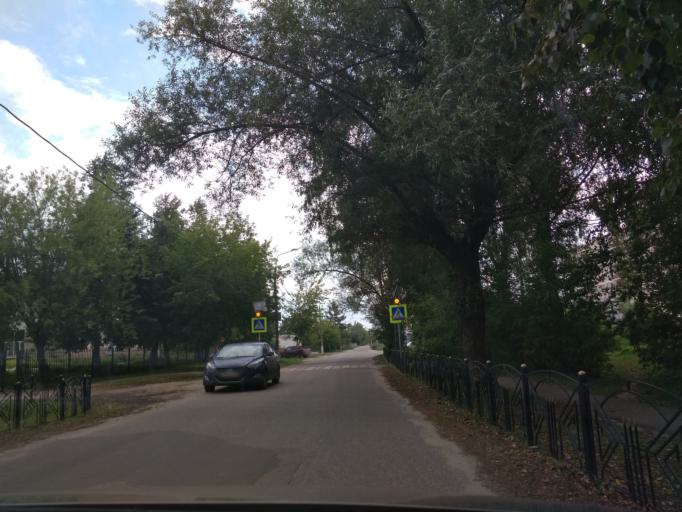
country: RU
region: Moskovskaya
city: Orekhovo-Zuyevo
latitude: 55.7898
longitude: 38.9300
